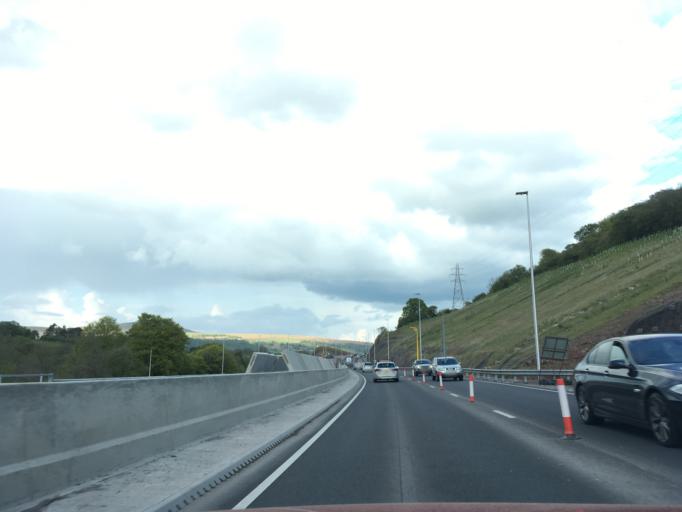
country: GB
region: Wales
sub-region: Monmouthshire
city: Gilwern
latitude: 51.8168
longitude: -3.1137
